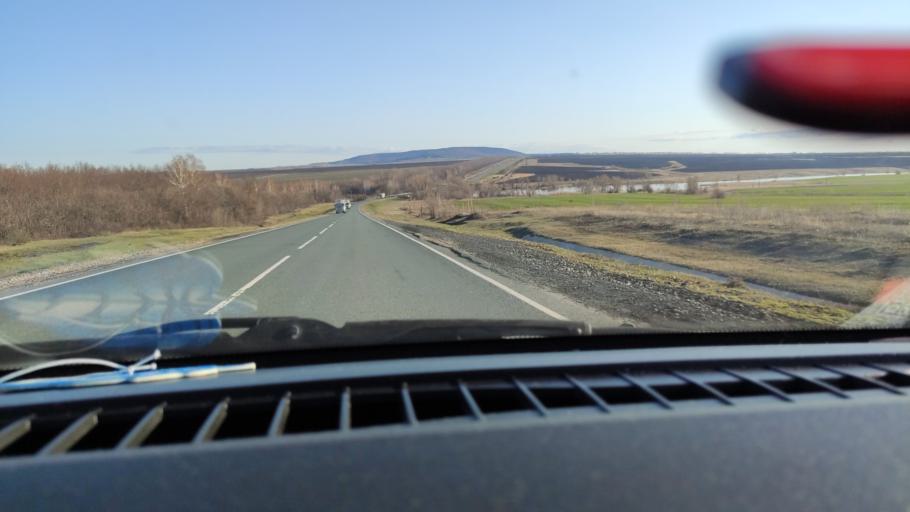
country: RU
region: Saratov
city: Alekseyevka
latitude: 52.2414
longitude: 47.9063
